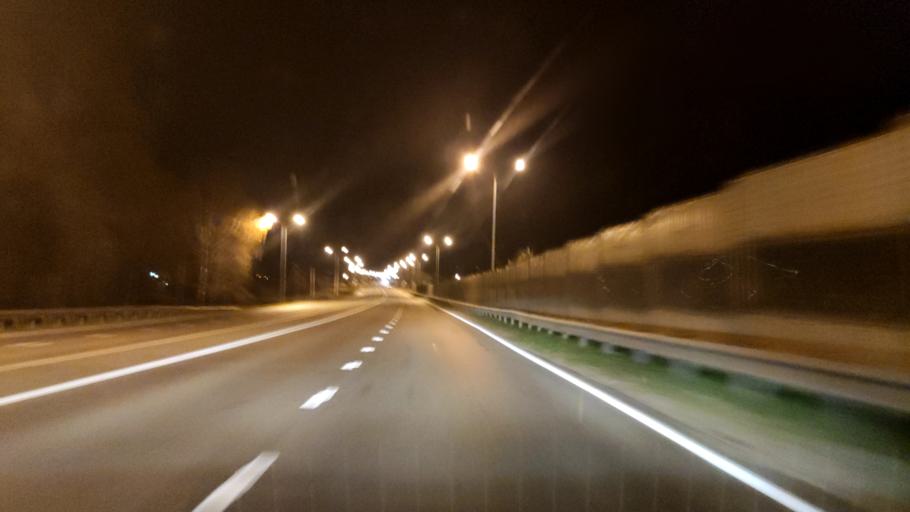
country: RU
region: Belgorod
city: Staryy Oskol
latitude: 51.3408
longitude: 37.7999
